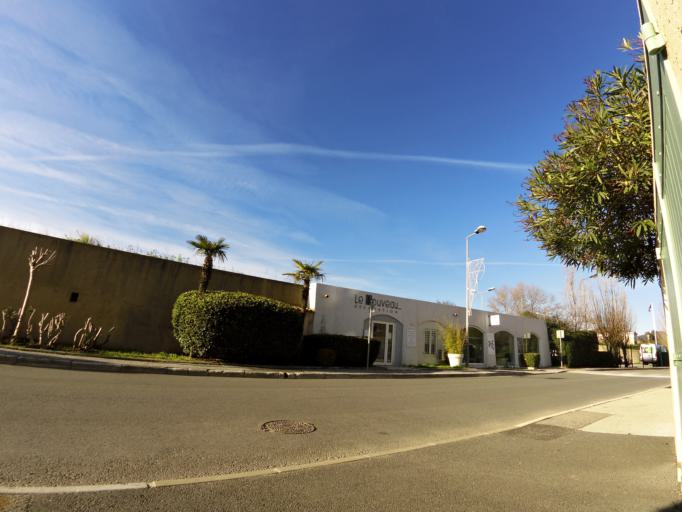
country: FR
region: Provence-Alpes-Cote d'Azur
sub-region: Departement du Var
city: Gassin
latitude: 43.2730
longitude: 6.5748
